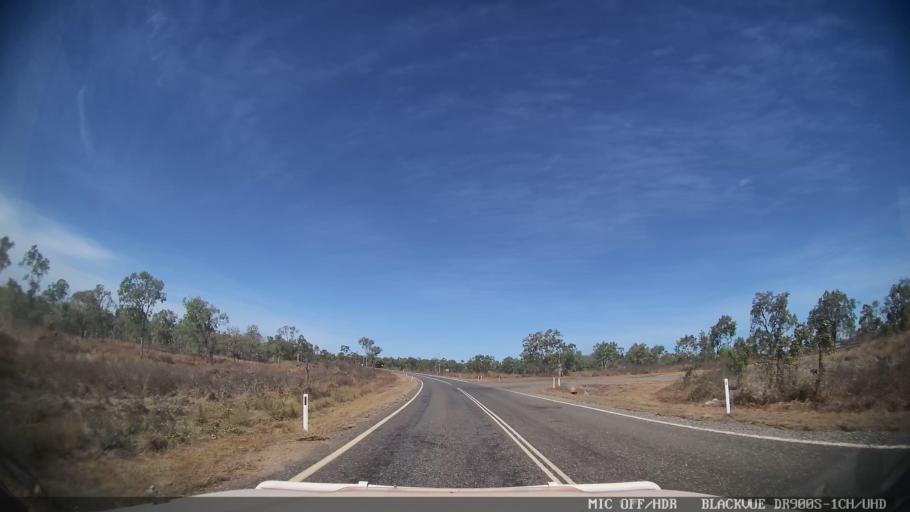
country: AU
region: Queensland
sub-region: Cook
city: Cooktown
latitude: -15.8648
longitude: 144.8051
